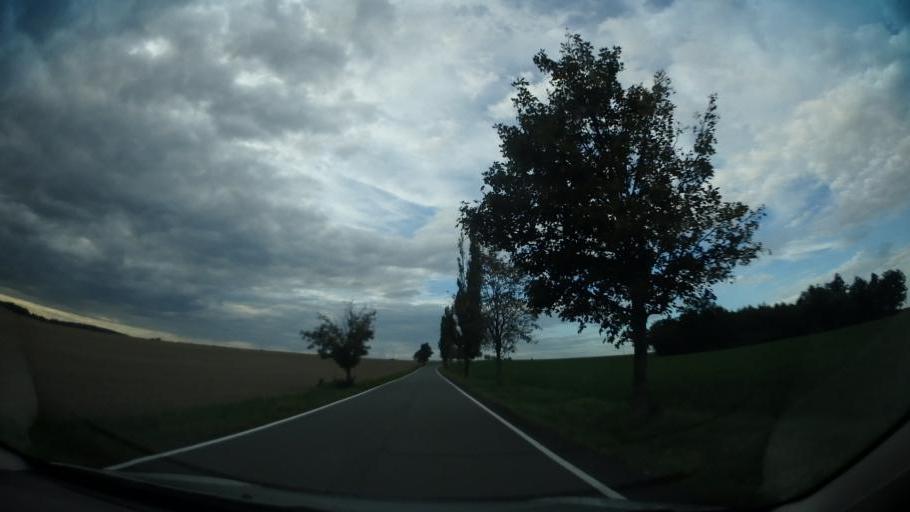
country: CZ
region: Olomoucky
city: Konice
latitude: 49.6157
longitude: 16.8921
